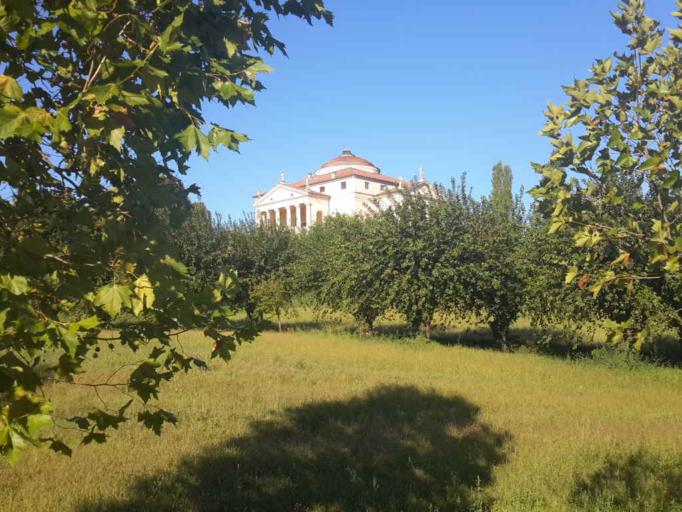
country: IT
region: Veneto
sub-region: Provincia di Vicenza
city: Vicenza
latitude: 45.5315
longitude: 11.5622
